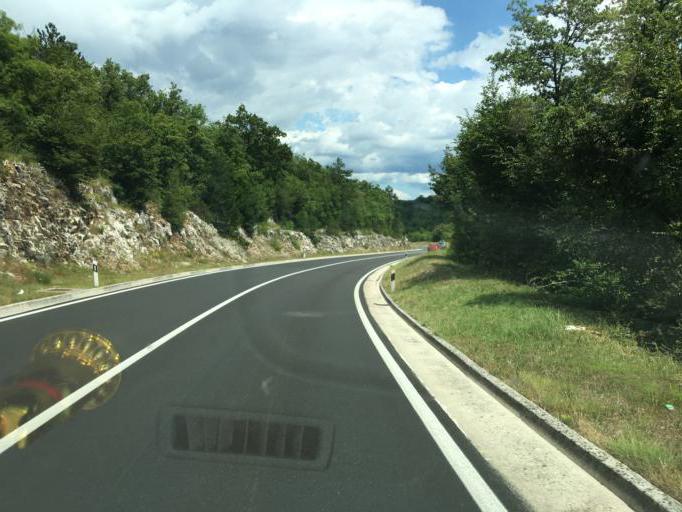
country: HR
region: Istarska
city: Pazin
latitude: 45.2462
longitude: 13.8768
